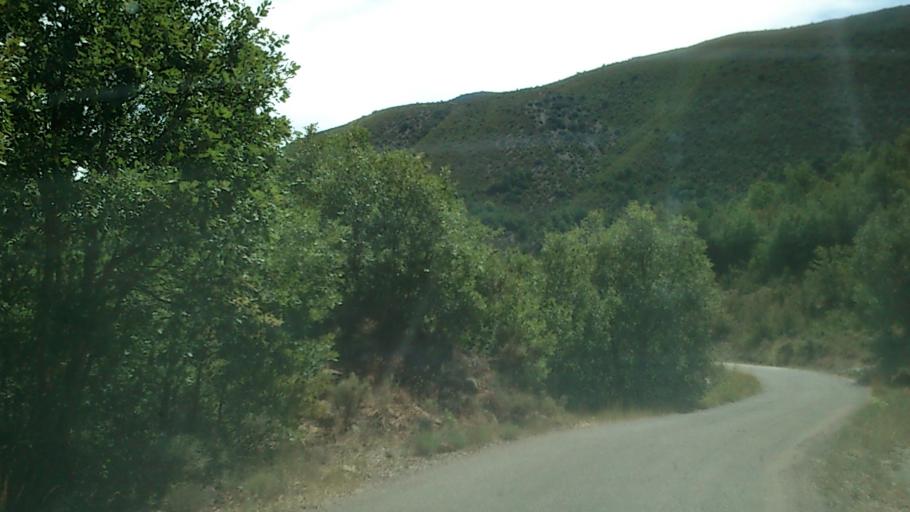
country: ES
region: Aragon
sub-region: Provincia de Huesca
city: Arguis
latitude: 42.3110
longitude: -0.3514
